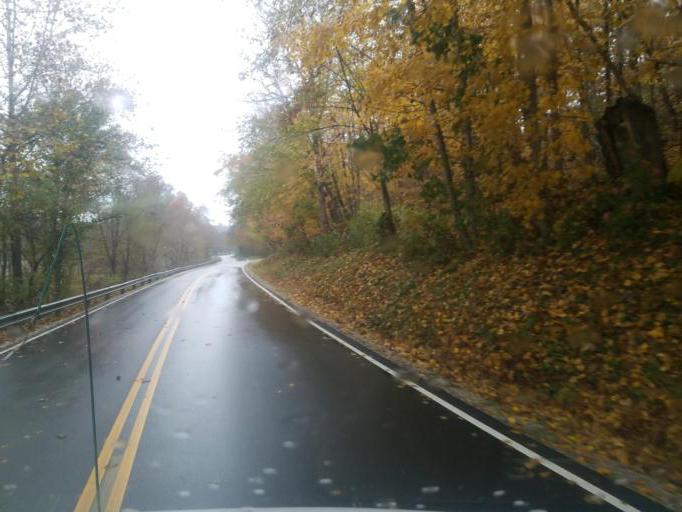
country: US
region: West Virginia
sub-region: Wood County
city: Blennerhassett
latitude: 39.3364
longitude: -81.6212
